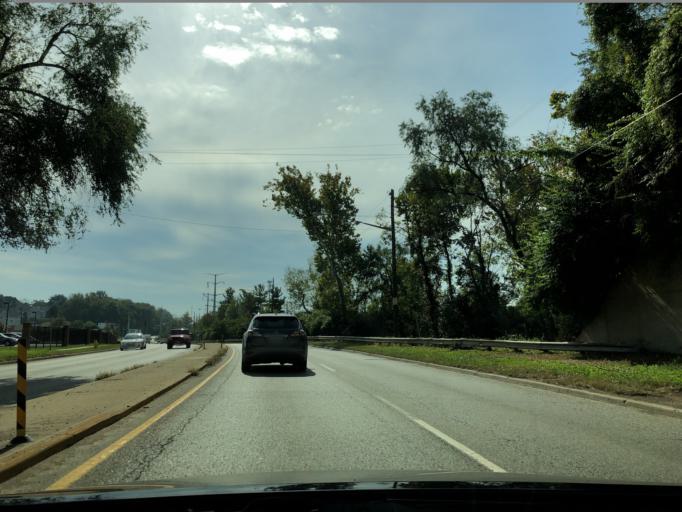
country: US
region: Ohio
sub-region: Hamilton County
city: Fairfax
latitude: 39.1567
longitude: -84.4062
